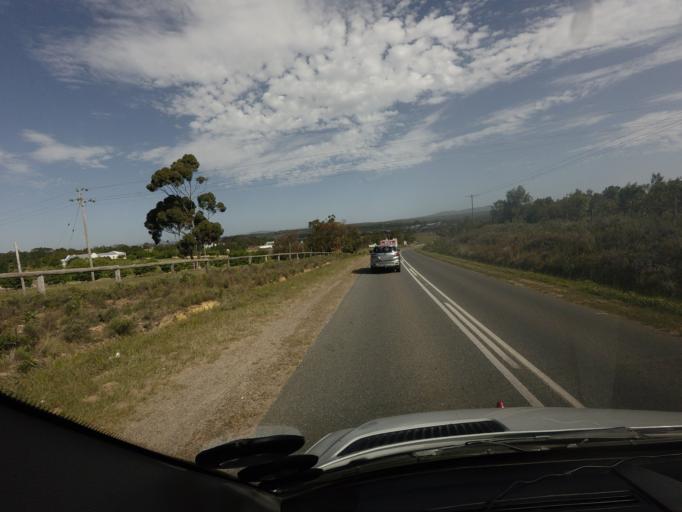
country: ZA
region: Western Cape
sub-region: Overberg District Municipality
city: Caledon
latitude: -34.4285
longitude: 19.4631
